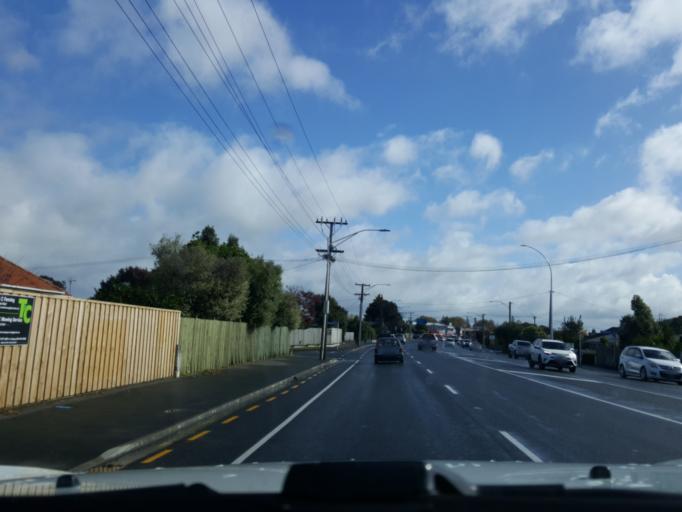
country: NZ
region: Waikato
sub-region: Hamilton City
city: Hamilton
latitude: -37.7666
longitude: 175.2570
